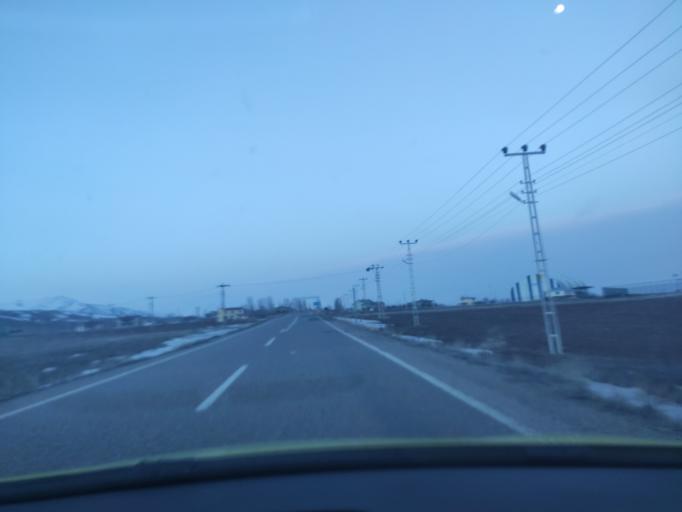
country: TR
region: Bayburt
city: Aydintepe
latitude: 40.3824
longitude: 40.1257
